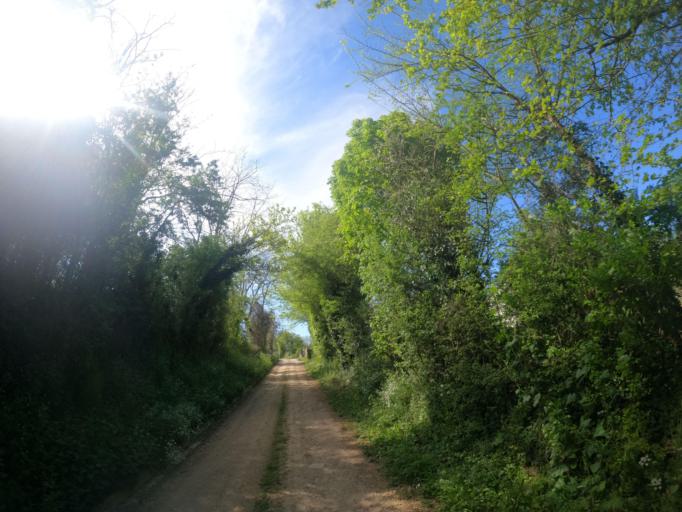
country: FR
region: Poitou-Charentes
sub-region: Departement des Deux-Sevres
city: Saint-Varent
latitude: 46.9136
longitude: -0.2099
